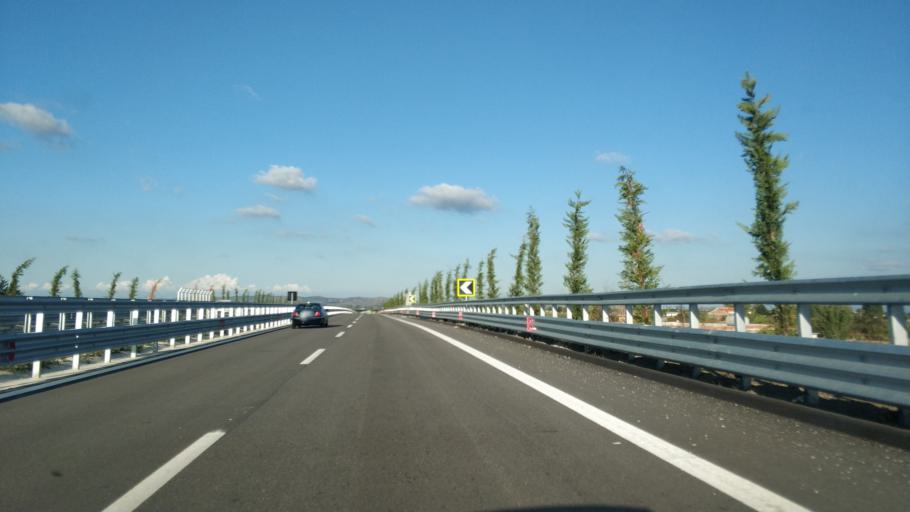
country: AL
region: Fier
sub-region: Rrethi i Fierit
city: Dermenas
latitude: 40.7421
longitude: 19.5007
